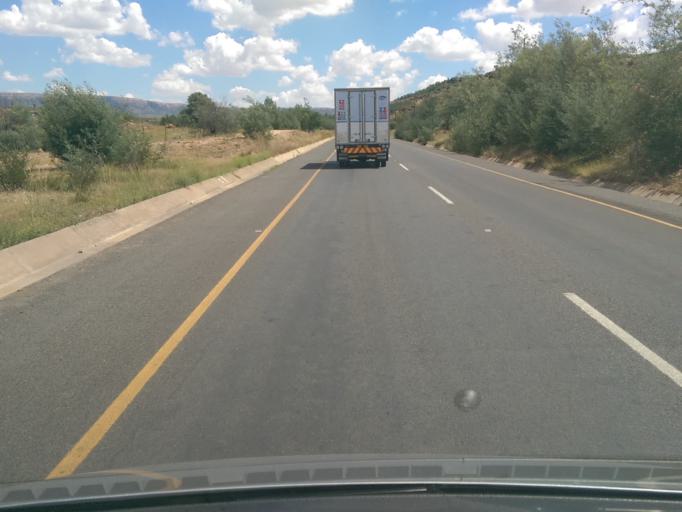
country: LS
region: Maseru
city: Maseru
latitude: -29.3947
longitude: 27.5400
